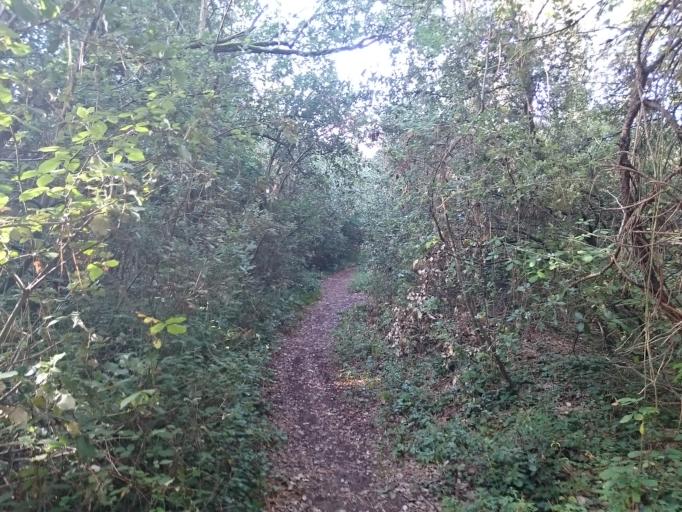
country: FR
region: Pays de la Loire
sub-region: Departement de la Vendee
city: Longeville-sur-Mer
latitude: 46.4006
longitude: -1.5038
